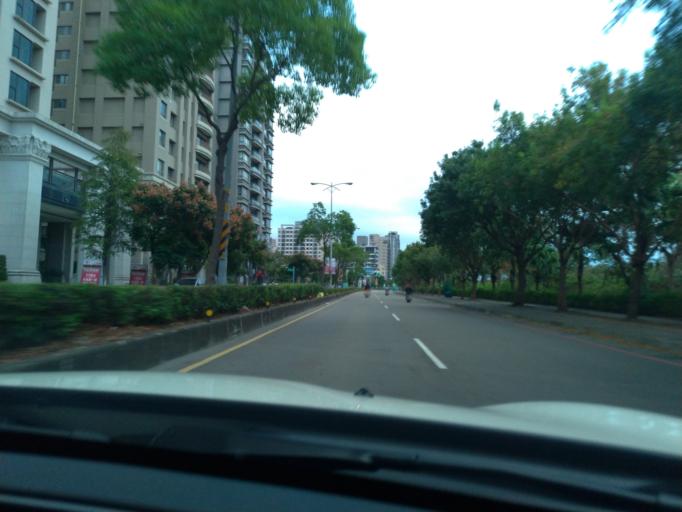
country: TW
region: Taiwan
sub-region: Hsinchu
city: Zhubei
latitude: 24.8050
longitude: 121.0281
